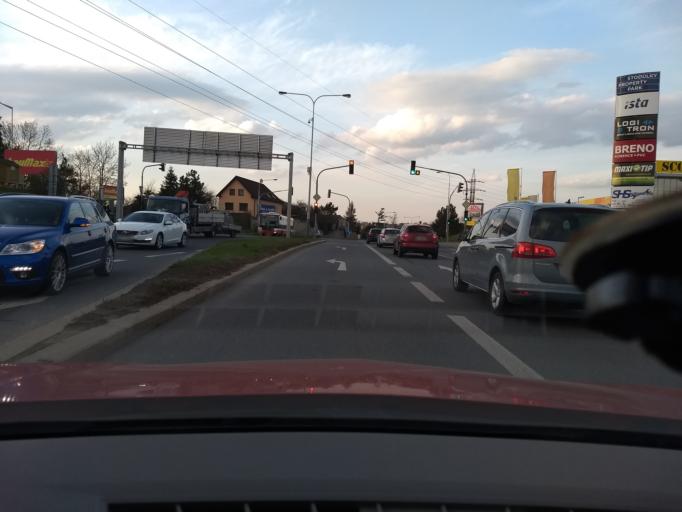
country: CZ
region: Central Bohemia
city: Hostivice
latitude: 50.0546
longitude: 14.3099
